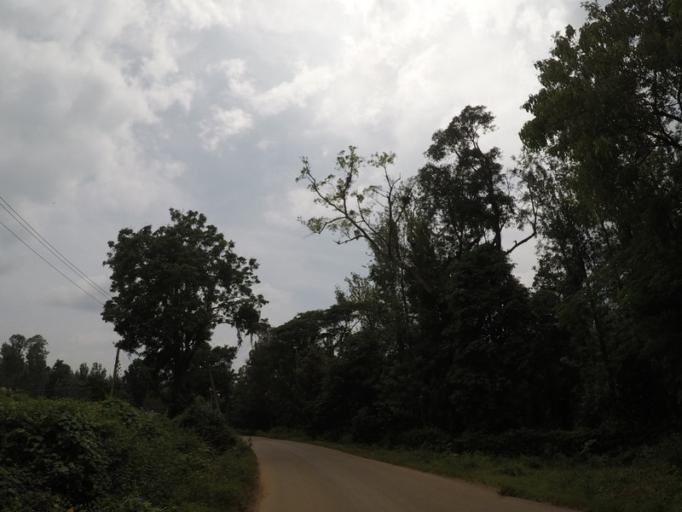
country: IN
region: Karnataka
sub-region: Chikmagalur
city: Chikmagalur
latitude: 13.4452
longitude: 75.8032
